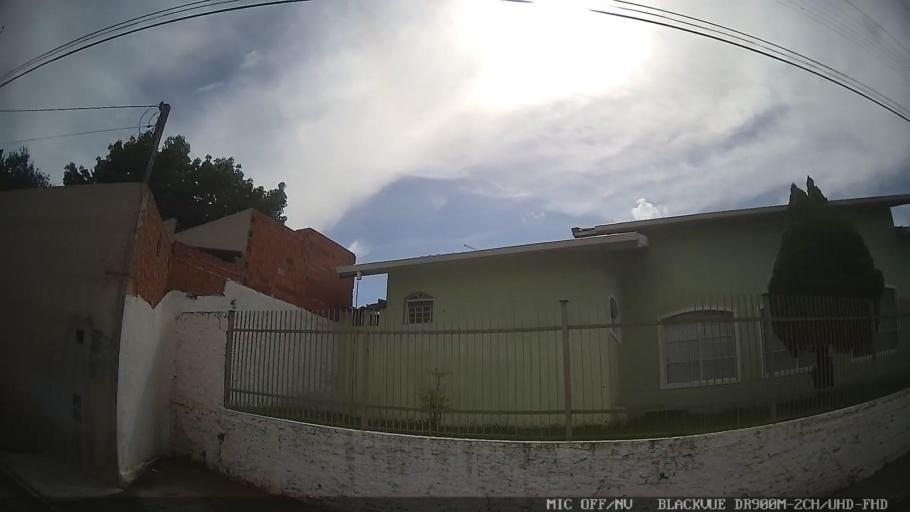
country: BR
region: Sao Paulo
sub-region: Conchas
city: Conchas
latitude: -23.0145
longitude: -48.0033
